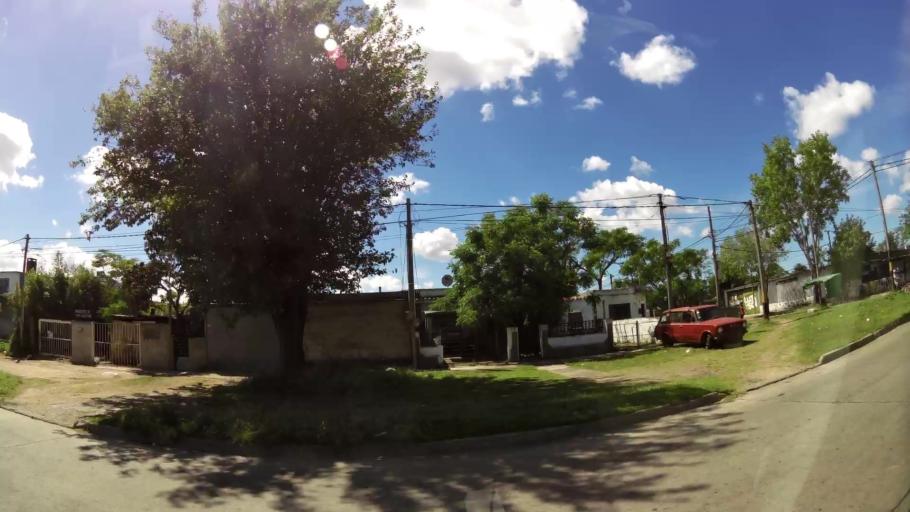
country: UY
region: Canelones
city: Paso de Carrasco
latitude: -34.8334
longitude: -56.1290
